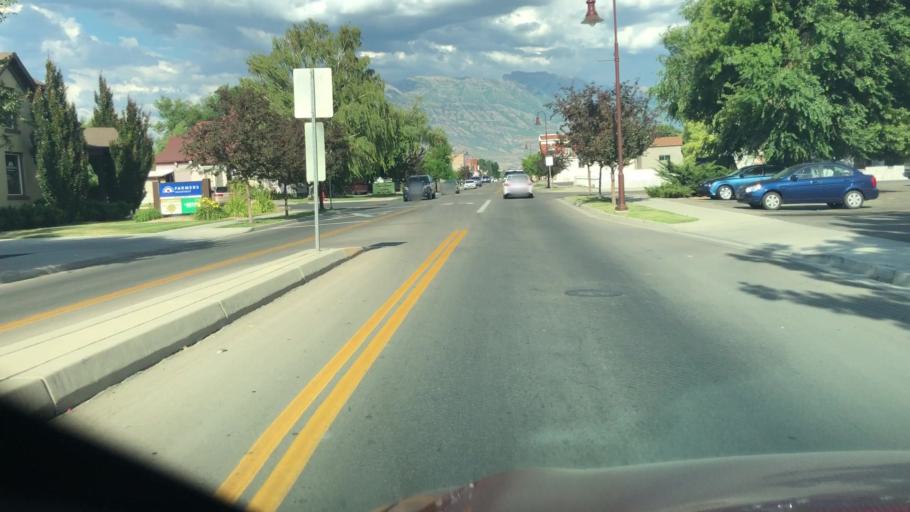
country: US
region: Utah
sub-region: Utah County
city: Lehi
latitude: 40.3877
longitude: -111.8545
